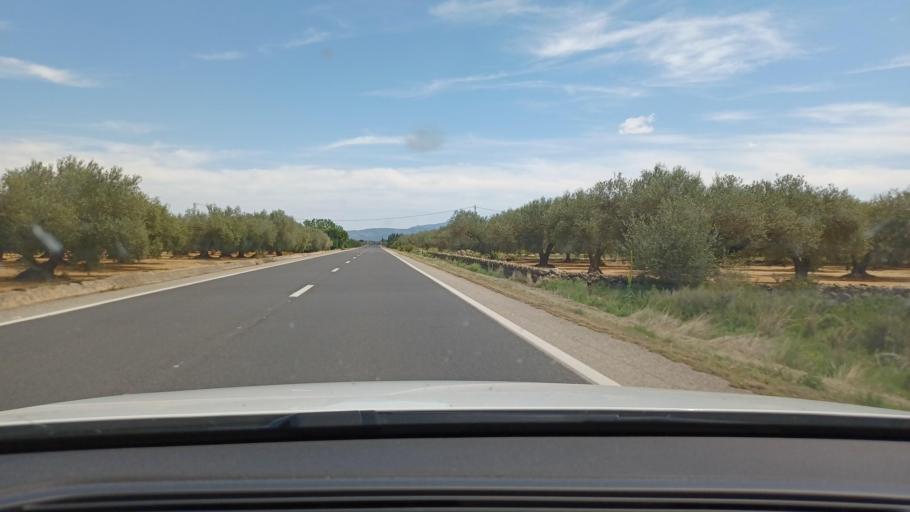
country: ES
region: Catalonia
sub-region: Provincia de Tarragona
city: Mas de Barberans
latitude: 40.6378
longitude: 0.3279
